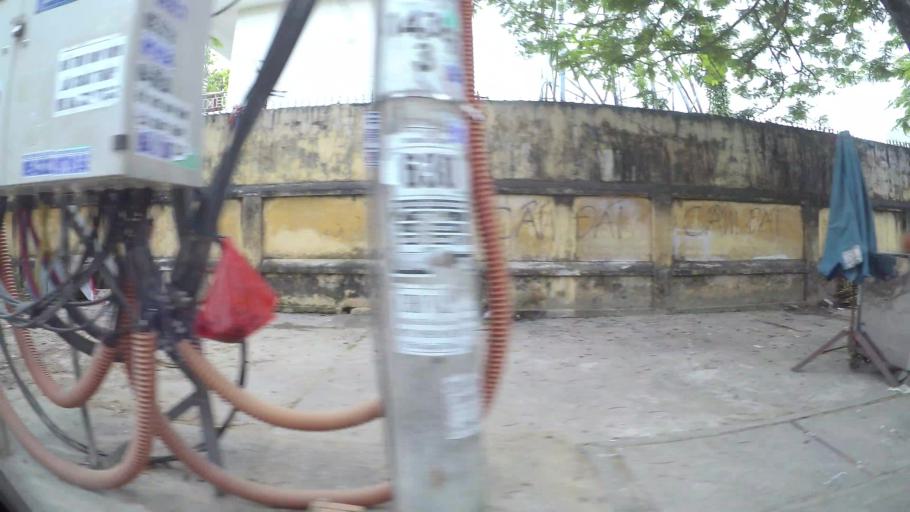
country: VN
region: Da Nang
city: Thanh Khe
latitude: 16.0603
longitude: 108.1865
